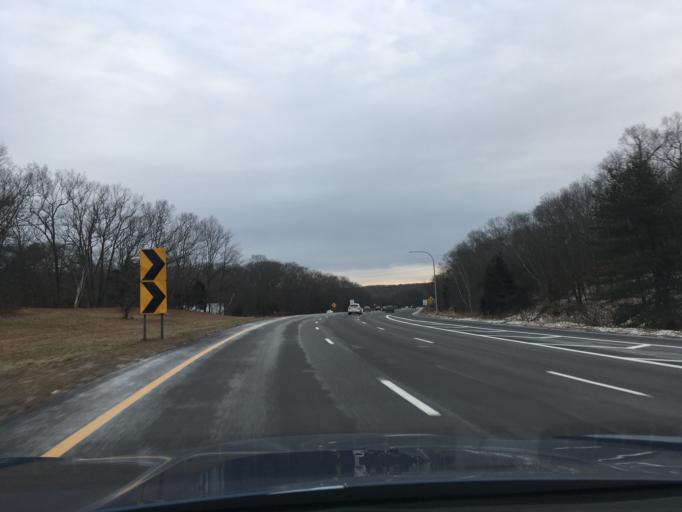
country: US
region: Rhode Island
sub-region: Kent County
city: East Greenwich
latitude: 41.6660
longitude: -71.4895
